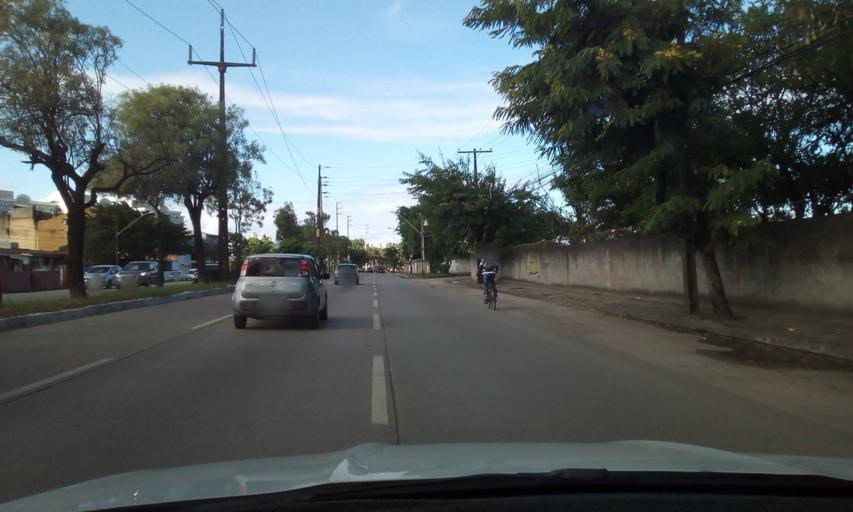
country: BR
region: Pernambuco
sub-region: Recife
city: Recife
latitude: -8.0613
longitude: -34.9290
